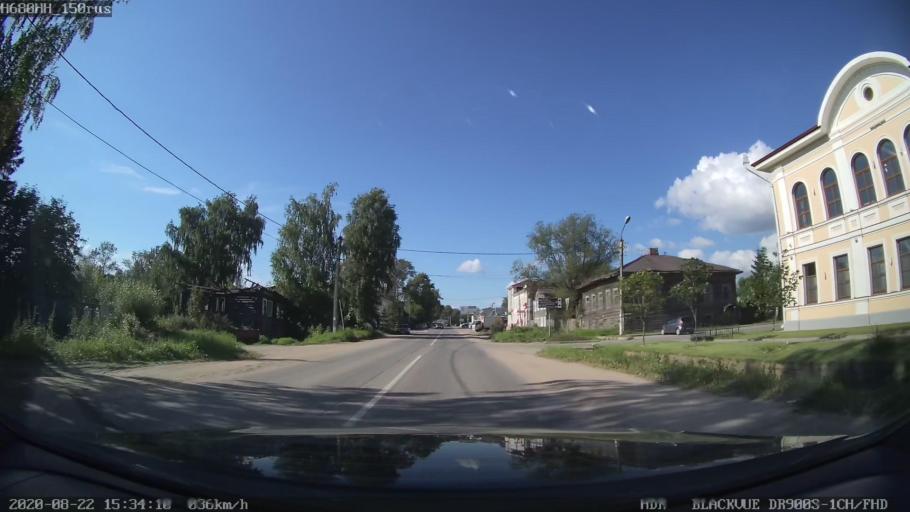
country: RU
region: Tverskaya
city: Bezhetsk
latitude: 57.7782
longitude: 36.6953
